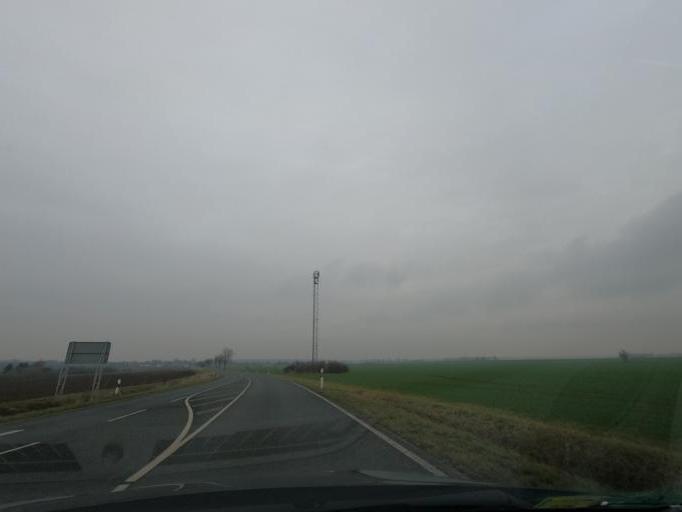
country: DE
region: Lower Saxony
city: Sickte
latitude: 52.1823
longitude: 10.5980
